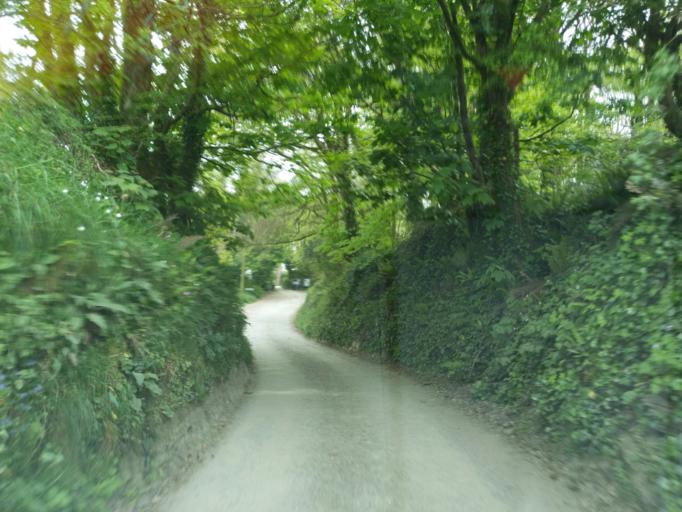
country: GB
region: England
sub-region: Cornwall
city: St Austell
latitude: 50.3083
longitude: -4.7646
